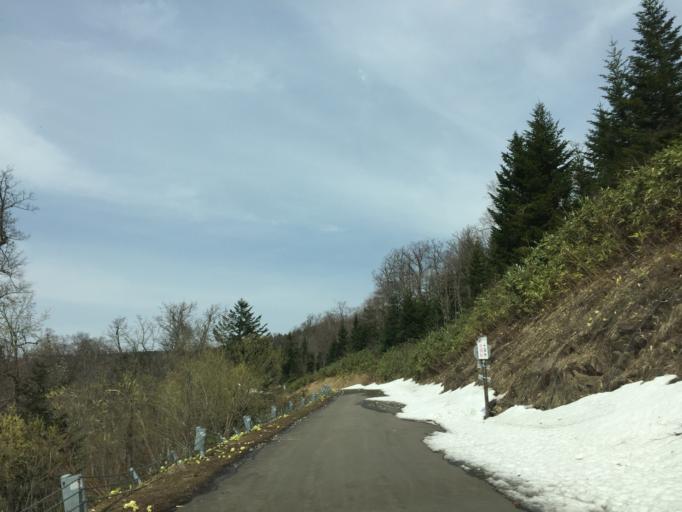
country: JP
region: Hokkaido
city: Akabira
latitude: 43.6057
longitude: 142.0676
